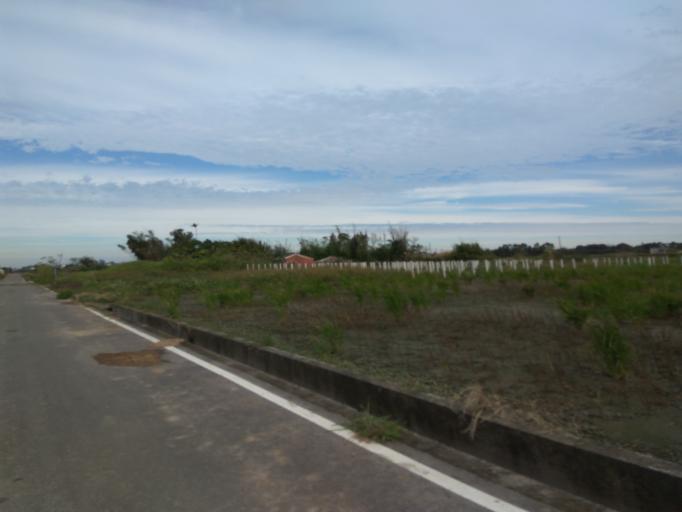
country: TW
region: Taiwan
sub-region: Hsinchu
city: Zhubei
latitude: 24.9499
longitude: 121.1057
